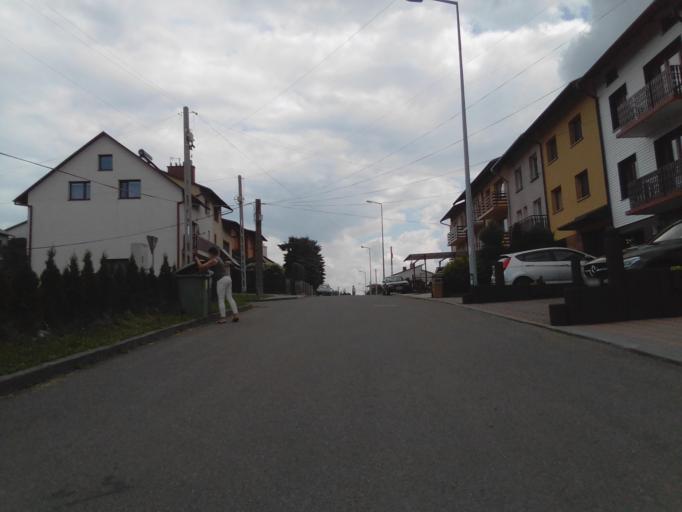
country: PL
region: Subcarpathian Voivodeship
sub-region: Powiat strzyzowski
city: Strzyzow
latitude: 49.8777
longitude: 21.7705
